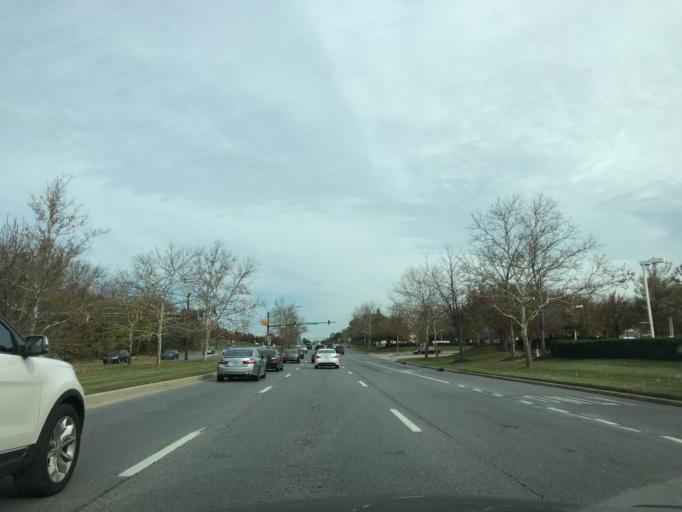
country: US
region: Maryland
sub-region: Howard County
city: Savage
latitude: 39.1828
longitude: -76.8211
